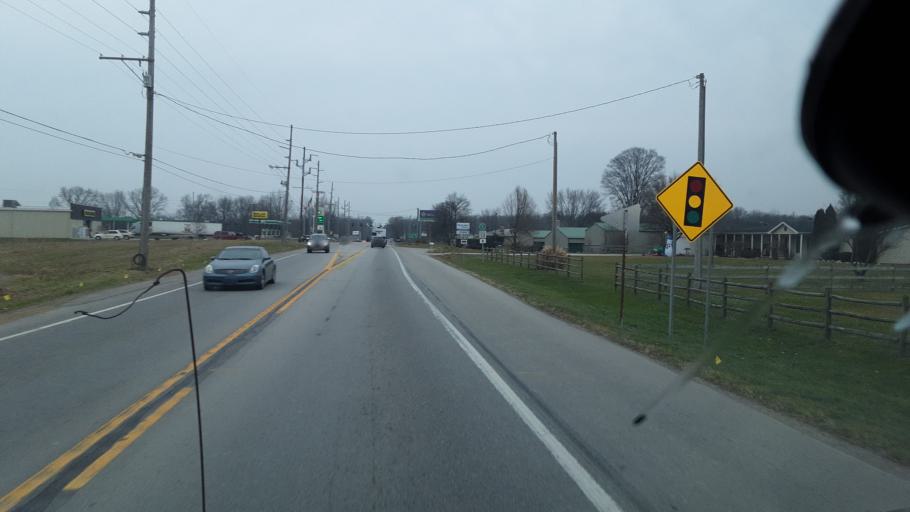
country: US
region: Indiana
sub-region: Elkhart County
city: Middlebury
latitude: 41.7232
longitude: -85.6844
